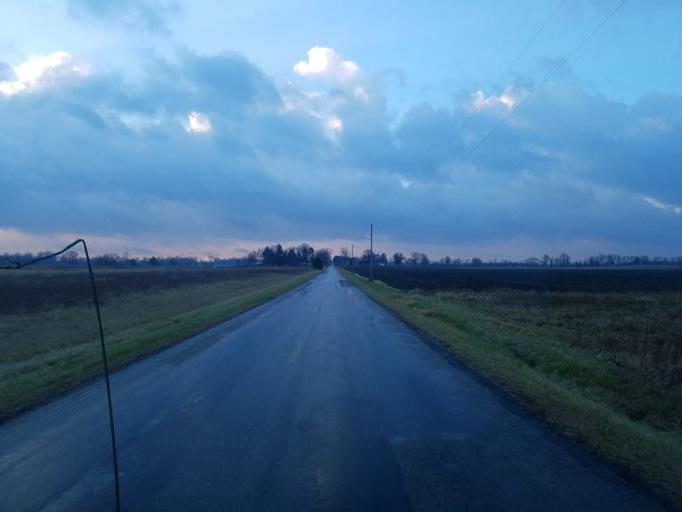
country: US
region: Ohio
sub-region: Marion County
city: Marion
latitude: 40.6270
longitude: -83.1887
